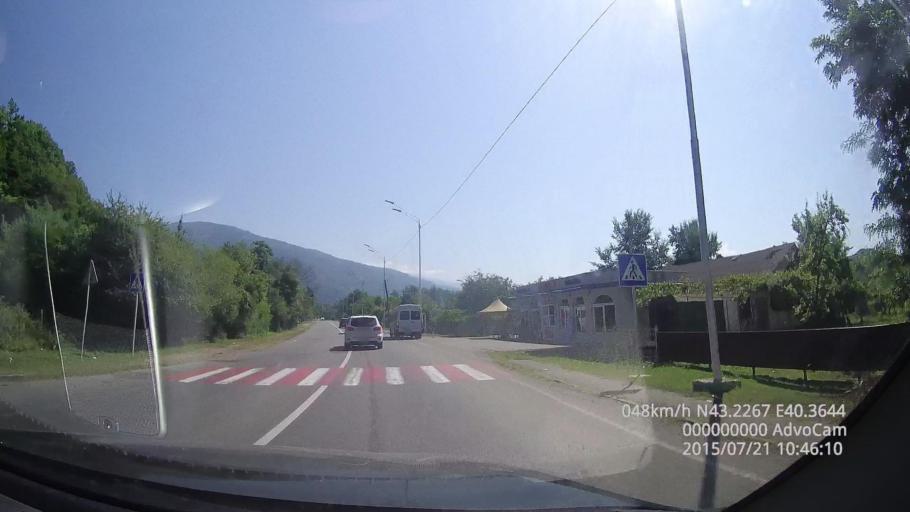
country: GE
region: Abkhazia
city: Bich'vinta
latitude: 43.2267
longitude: 40.3645
